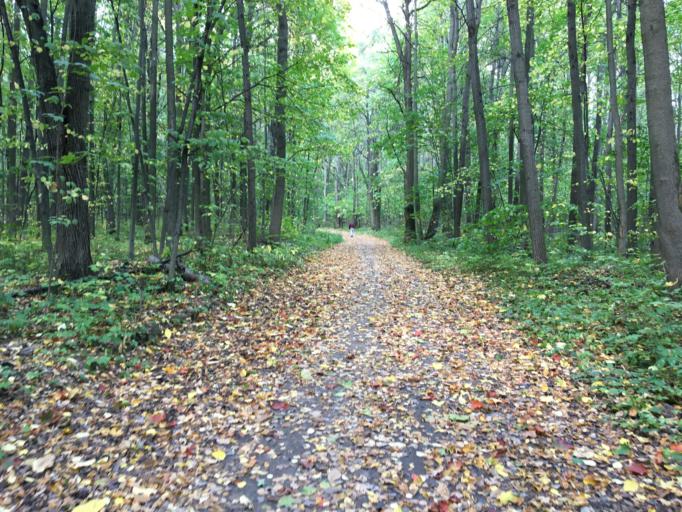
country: RU
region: Nizjnij Novgorod
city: Nizhniy Novgorod
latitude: 56.2691
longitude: 44.0081
